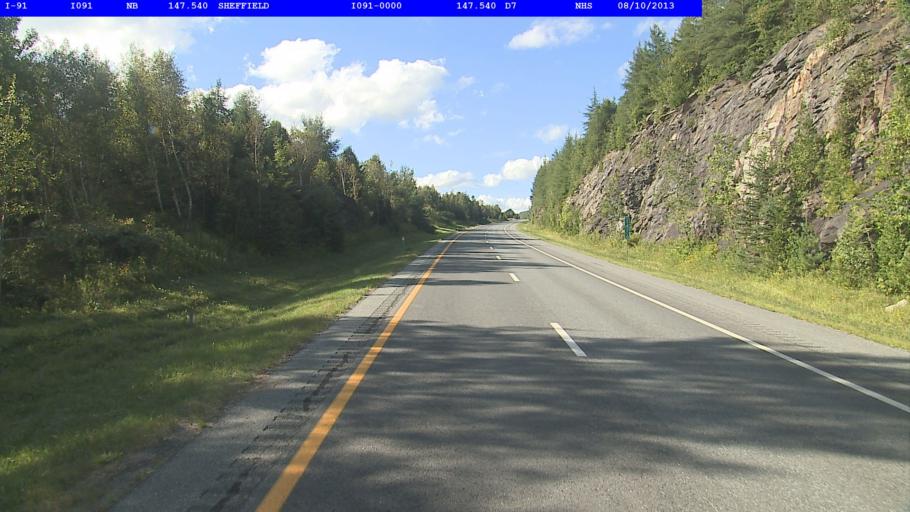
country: US
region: Vermont
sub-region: Caledonia County
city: Lyndonville
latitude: 44.6293
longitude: -72.1289
